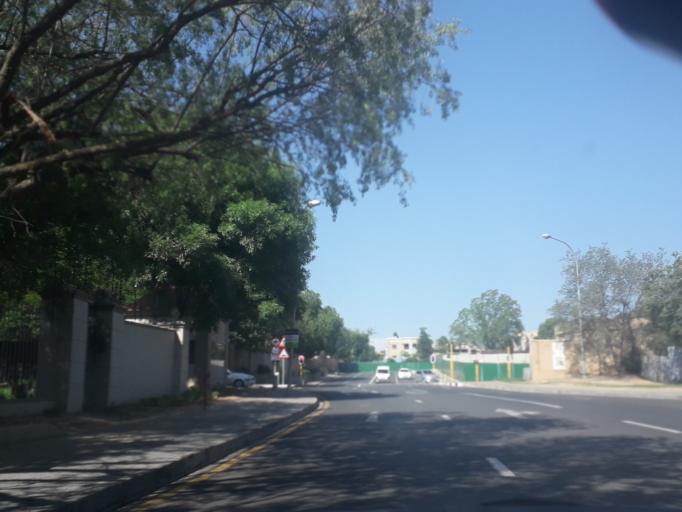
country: ZA
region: Gauteng
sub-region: City of Johannesburg Metropolitan Municipality
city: Johannesburg
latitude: -26.1137
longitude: 28.0542
